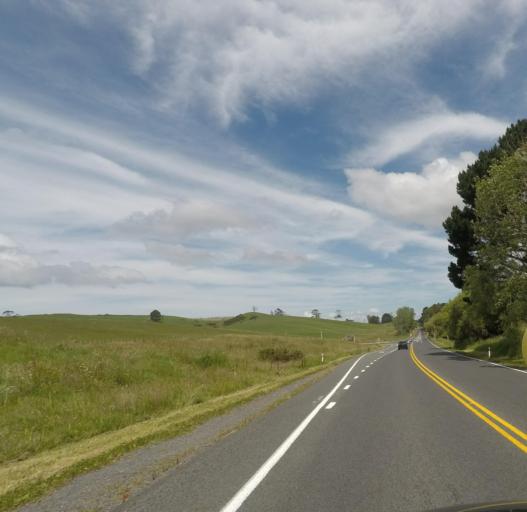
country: NZ
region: Auckland
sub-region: Auckland
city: Rothesay Bay
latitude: -36.6641
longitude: 174.6770
